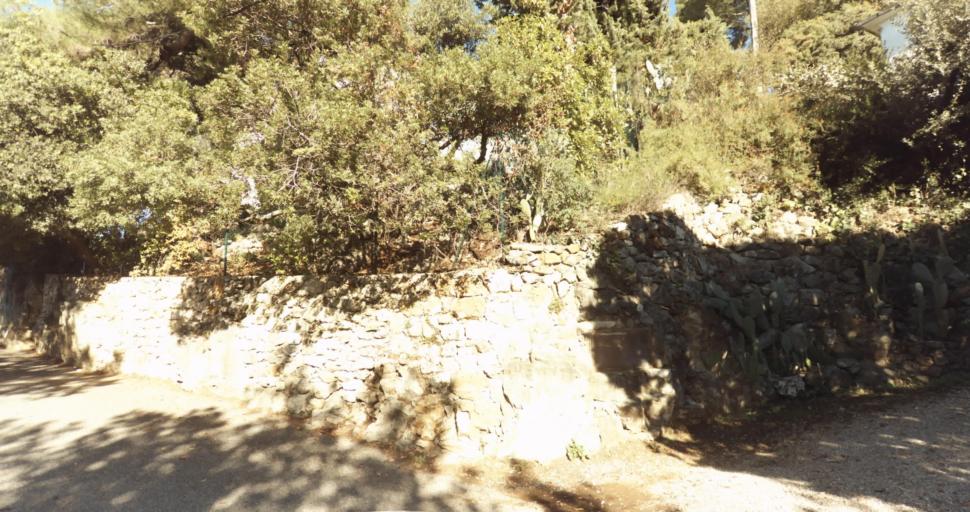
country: FR
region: Provence-Alpes-Cote d'Azur
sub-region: Departement des Alpes-Maritimes
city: Vence
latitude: 43.7156
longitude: 7.1117
